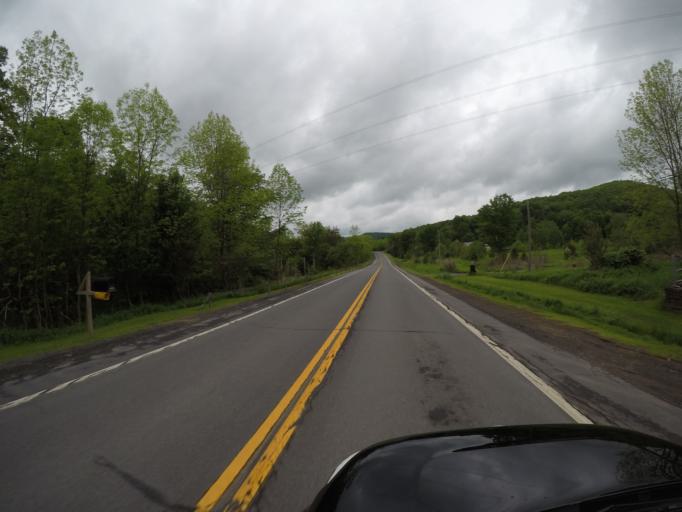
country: US
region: New York
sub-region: Delaware County
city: Delhi
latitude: 42.2516
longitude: -74.8465
